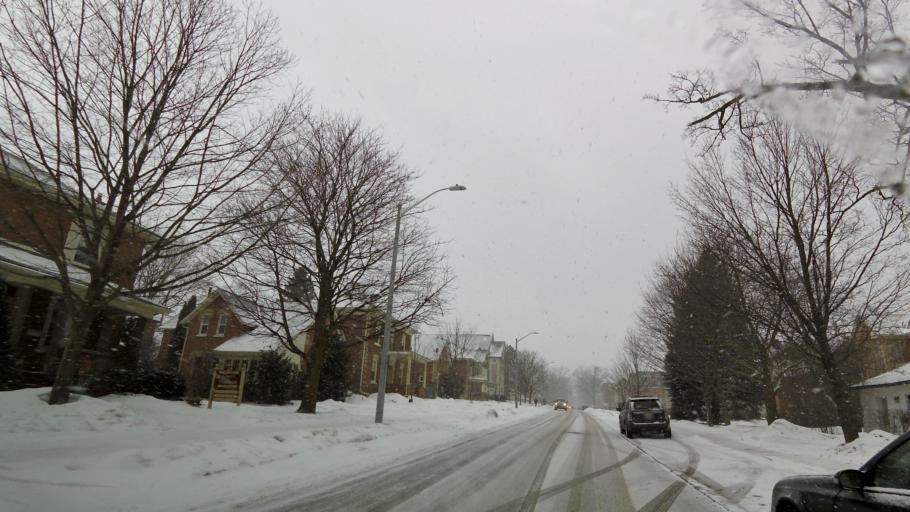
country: CA
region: Ontario
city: Orangeville
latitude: 43.9208
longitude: -80.0954
